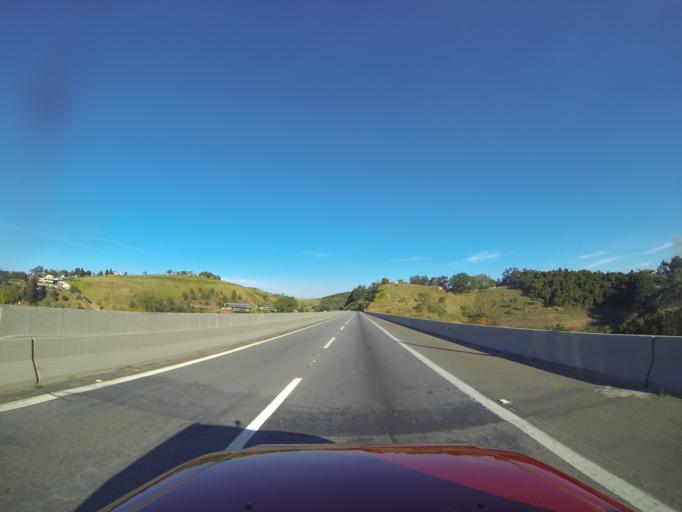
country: BR
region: Sao Paulo
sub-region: Santa Isabel
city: Santa Isabel
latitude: -23.2177
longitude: -46.1462
